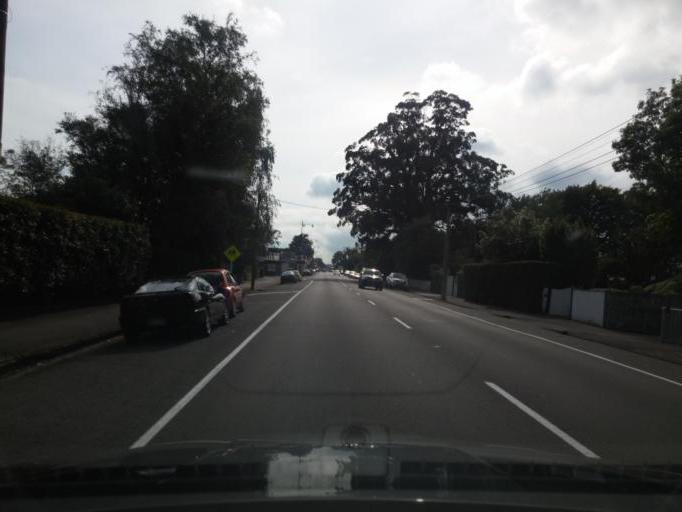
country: NZ
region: Wellington
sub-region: Masterton District
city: Masterton
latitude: -41.0834
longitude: 175.4570
